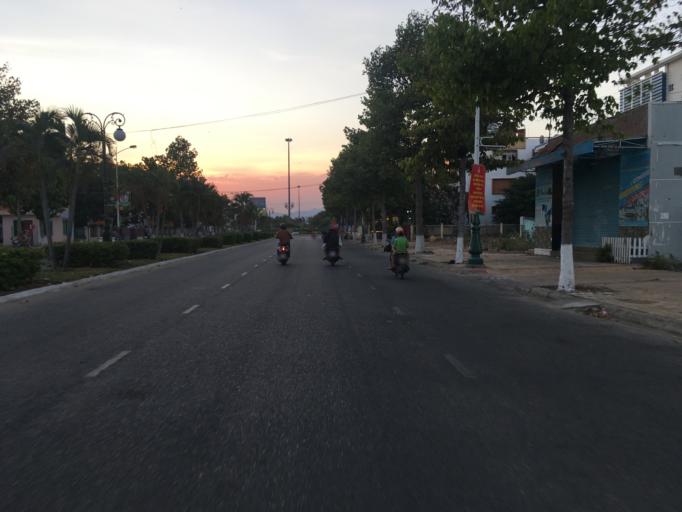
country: VN
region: Ninh Thuan
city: Phan Rang-Thap Cham
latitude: 11.5649
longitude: 109.0033
